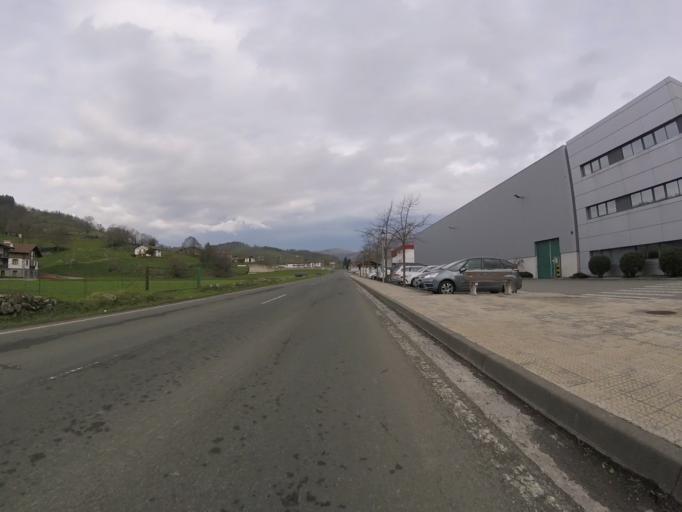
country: ES
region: Basque Country
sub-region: Provincia de Guipuzcoa
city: Albiztur
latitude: 43.1342
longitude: -2.1595
